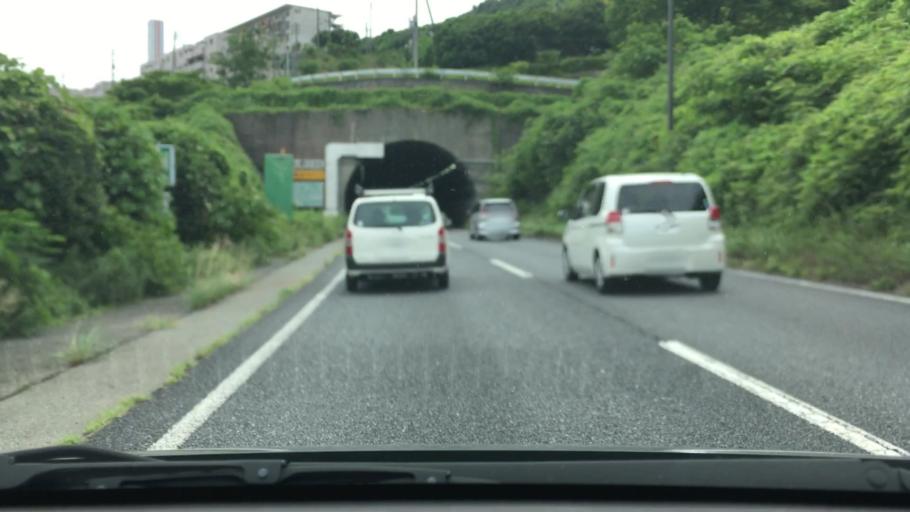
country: JP
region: Hiroshima
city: Hiroshima-shi
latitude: 34.3850
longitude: 132.3945
